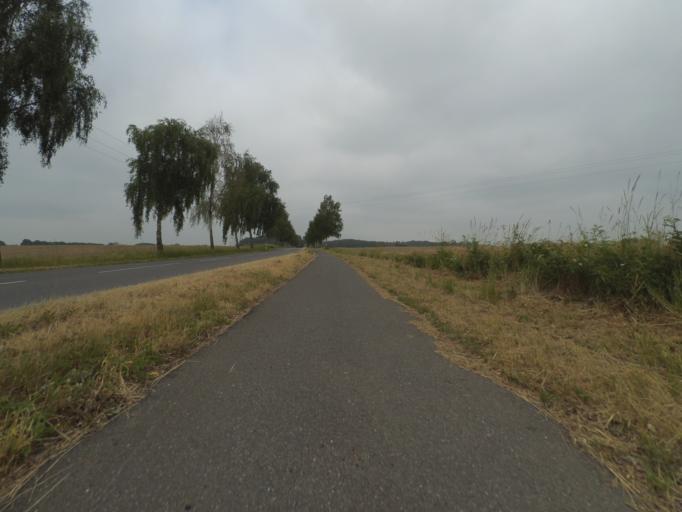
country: DE
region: Mecklenburg-Vorpommern
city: Plau am See
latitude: 53.4945
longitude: 12.1990
